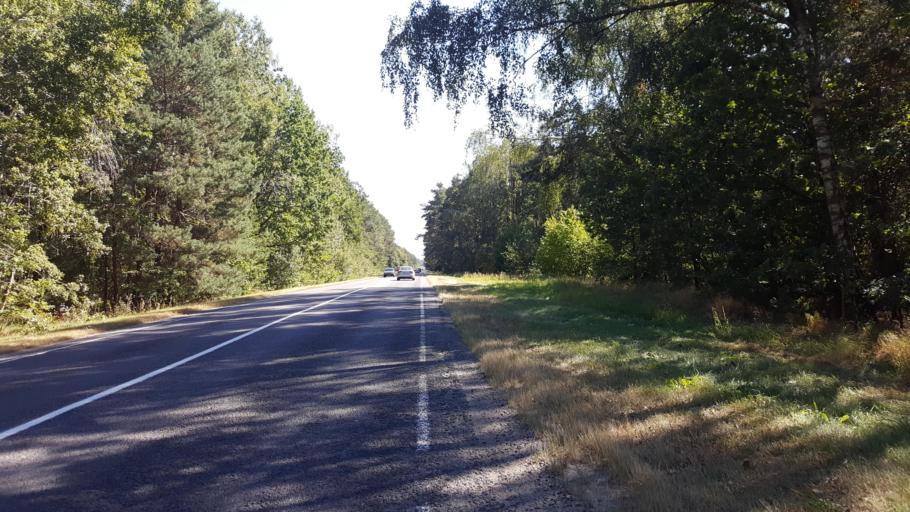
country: PL
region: Lublin Voivodeship
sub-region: Powiat bialski
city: Terespol
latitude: 52.2286
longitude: 23.5171
